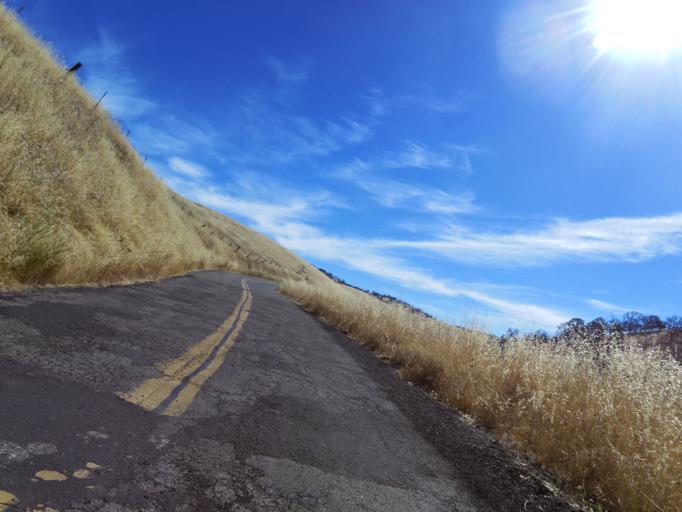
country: US
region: California
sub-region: Mariposa County
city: Mariposa
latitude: 37.3367
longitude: -119.9635
